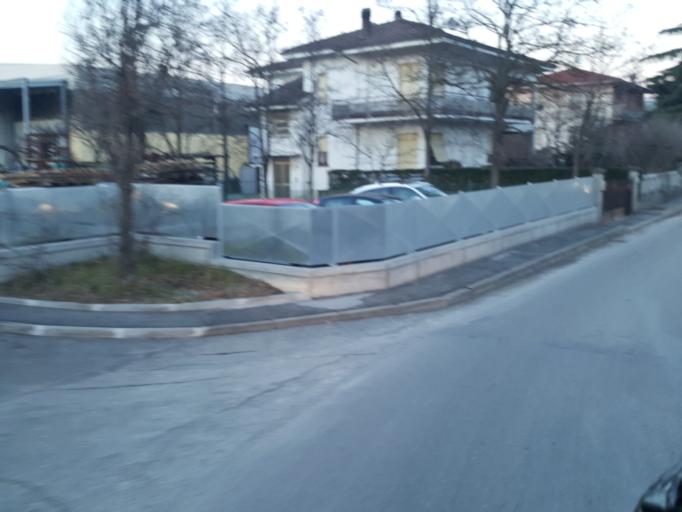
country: IT
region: Emilia-Romagna
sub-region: Provincia di Parma
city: Fornovo di Taro
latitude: 44.6965
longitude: 10.1048
